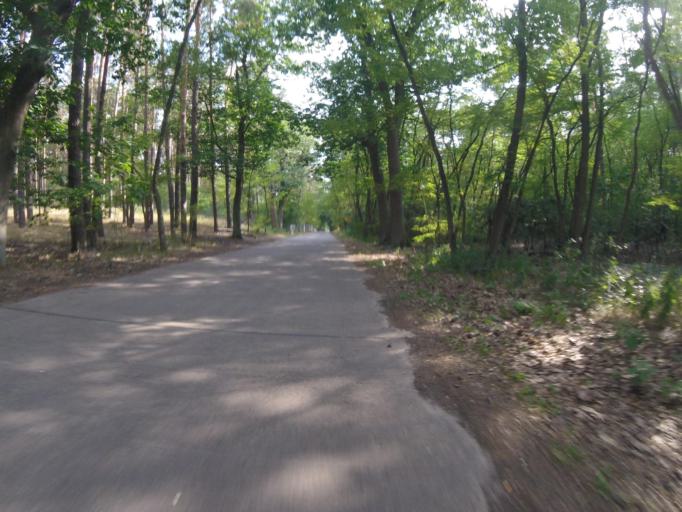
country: DE
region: Brandenburg
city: Munchehofe
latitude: 52.2636
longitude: 13.8030
